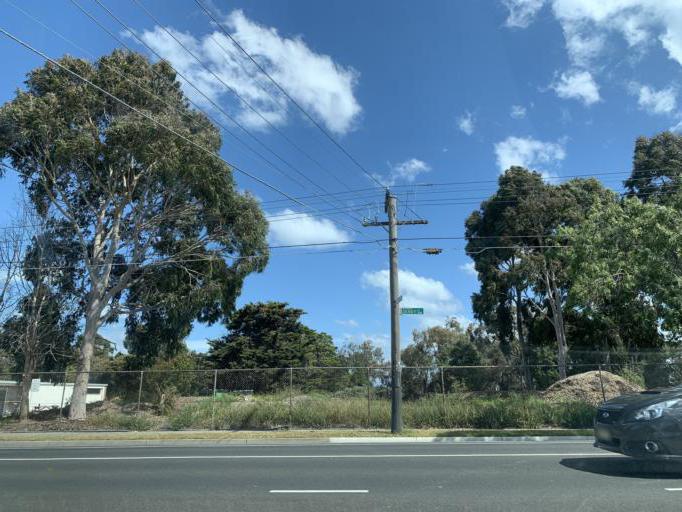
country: AU
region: Victoria
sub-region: Bayside
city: North Brighton
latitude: -37.9218
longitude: 145.0150
